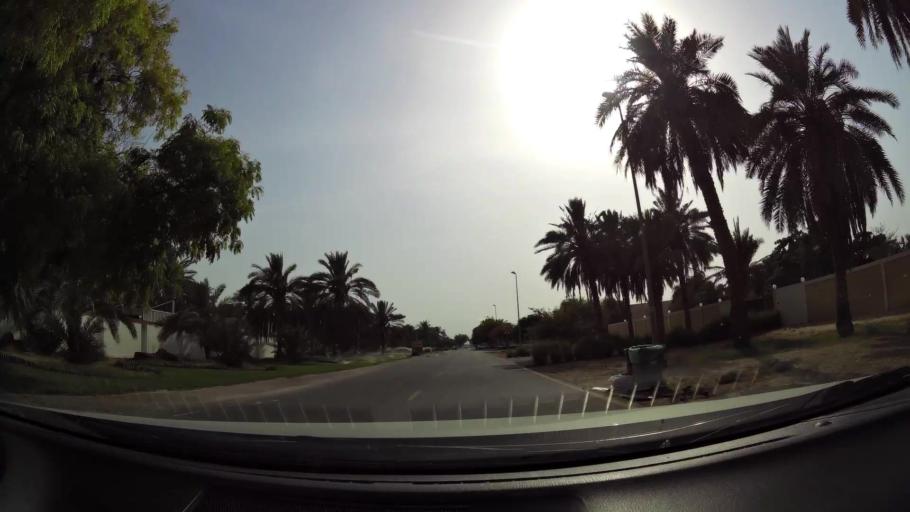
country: AE
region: Ash Shariqah
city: Sharjah
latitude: 25.2494
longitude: 55.4240
